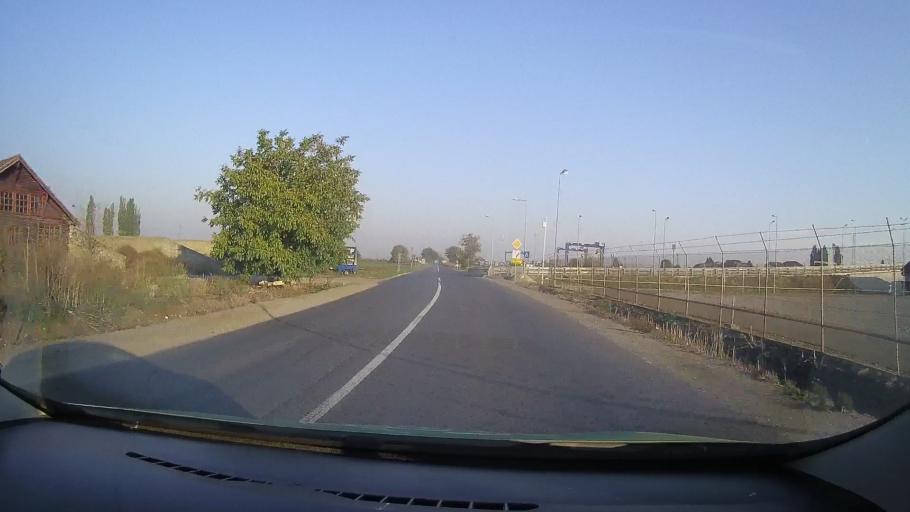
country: RO
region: Arad
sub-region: Comuna Curtici
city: Curtici
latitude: 46.3365
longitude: 21.2974
